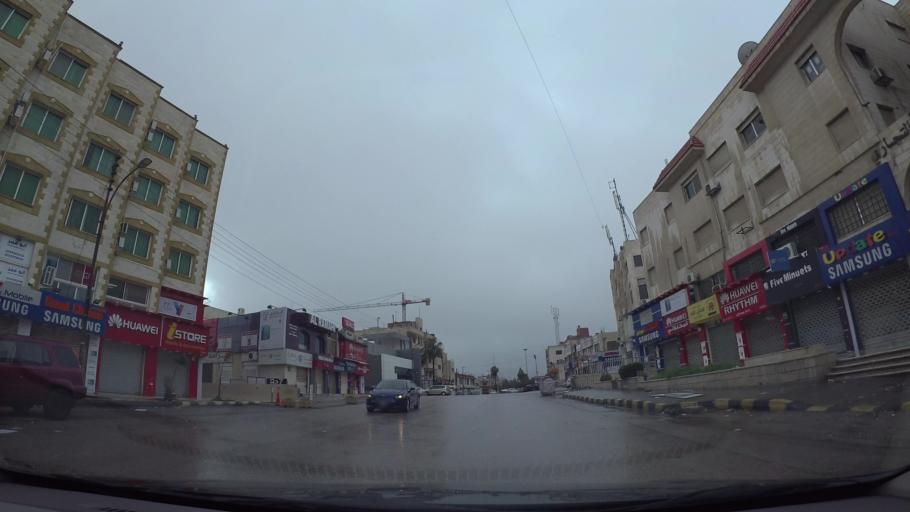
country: JO
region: Amman
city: Wadi as Sir
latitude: 31.9620
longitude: 35.8578
